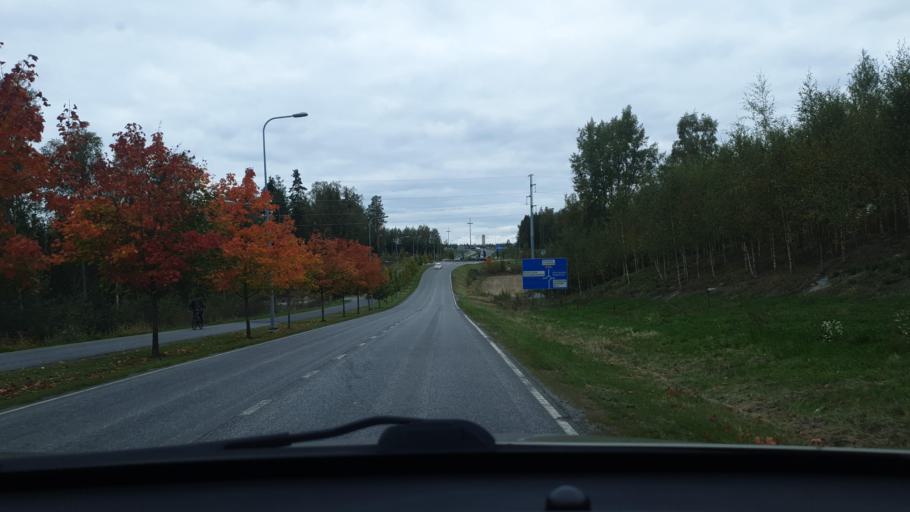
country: FI
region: Ostrobothnia
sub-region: Vaasa
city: Korsholm
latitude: 63.1081
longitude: 21.6686
